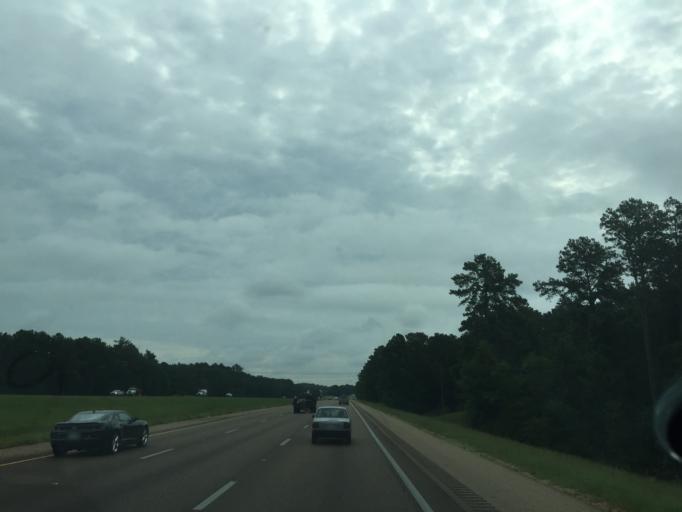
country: US
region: Mississippi
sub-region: Rankin County
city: Pearl
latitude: 32.2662
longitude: -90.1008
